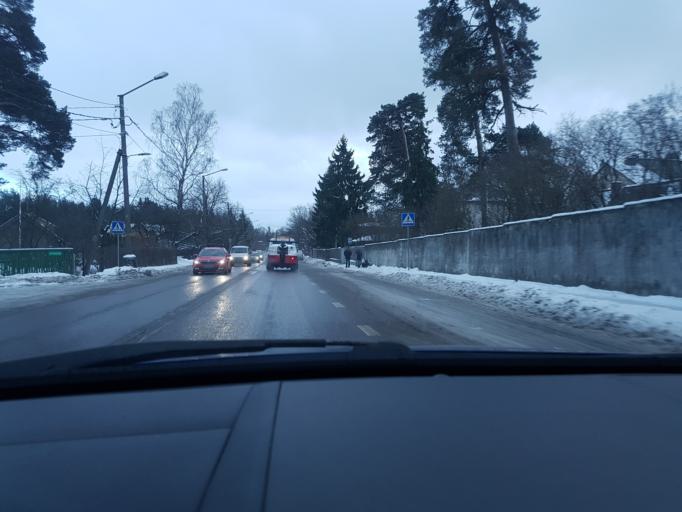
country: EE
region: Harju
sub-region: Tallinna linn
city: Tallinn
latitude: 59.3919
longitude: 24.7281
